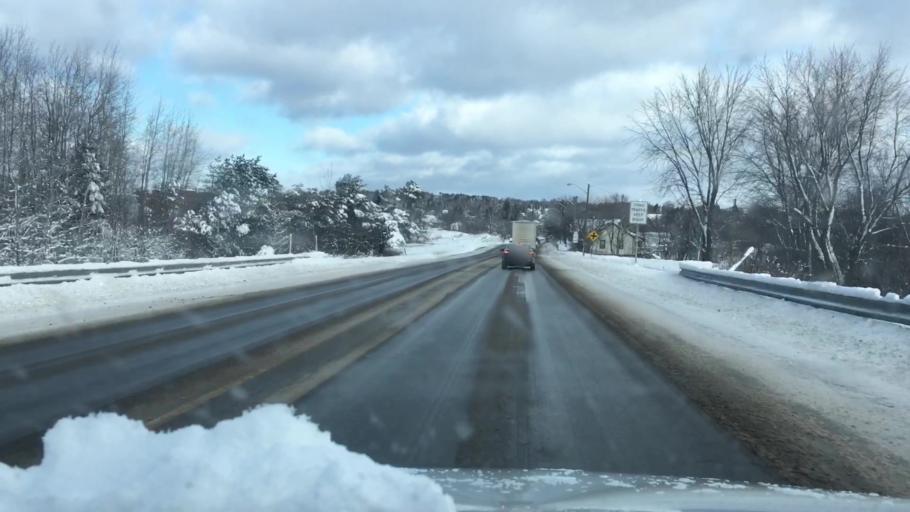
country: US
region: Maine
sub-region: Aroostook County
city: Caribou
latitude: 46.8506
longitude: -68.0051
